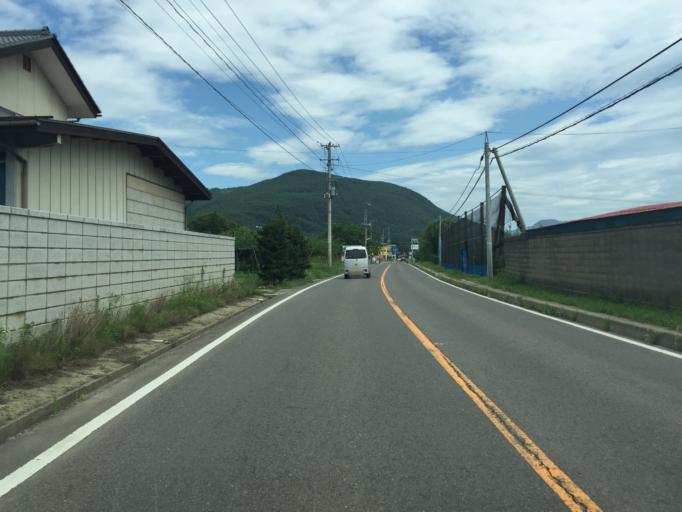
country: JP
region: Fukushima
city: Fukushima-shi
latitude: 37.7948
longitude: 140.4007
